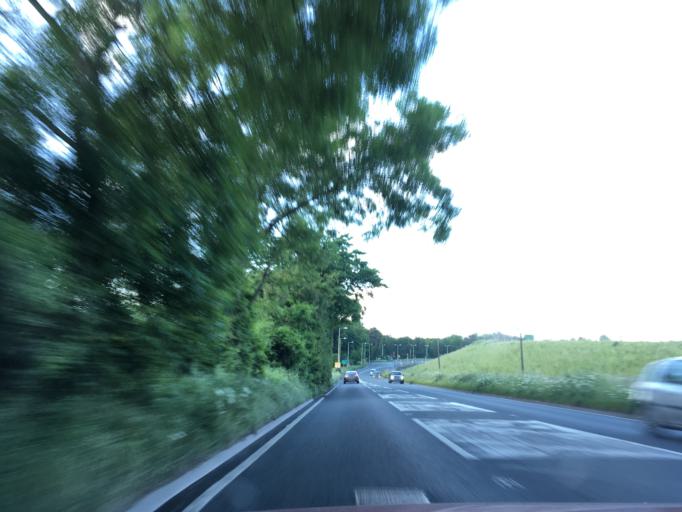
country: GB
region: England
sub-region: North Somerset
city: Winford
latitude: 51.4033
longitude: -2.6707
